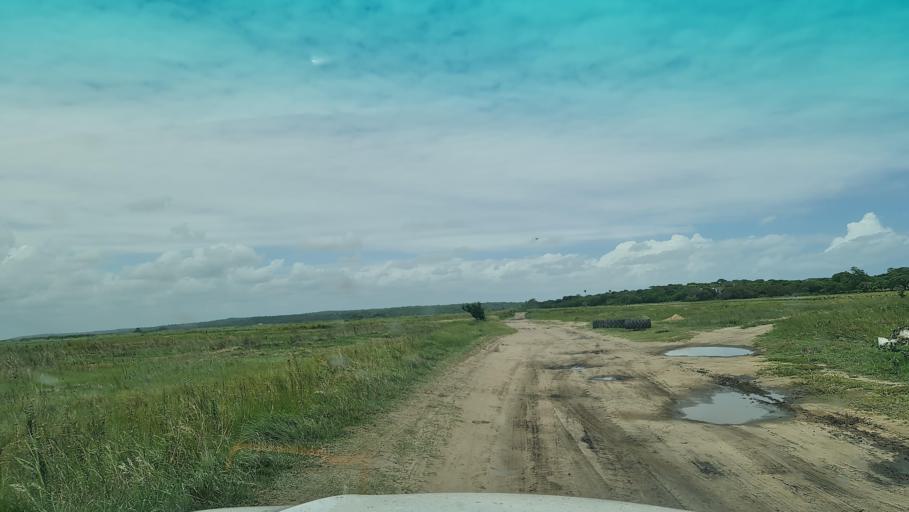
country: MZ
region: Maputo
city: Manhica
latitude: -25.5258
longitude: 32.8552
